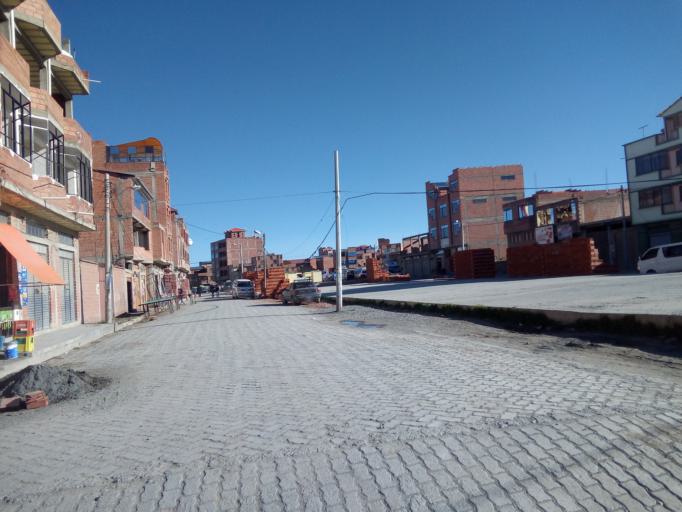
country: BO
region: La Paz
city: Achacachi
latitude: -16.0435
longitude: -68.6872
